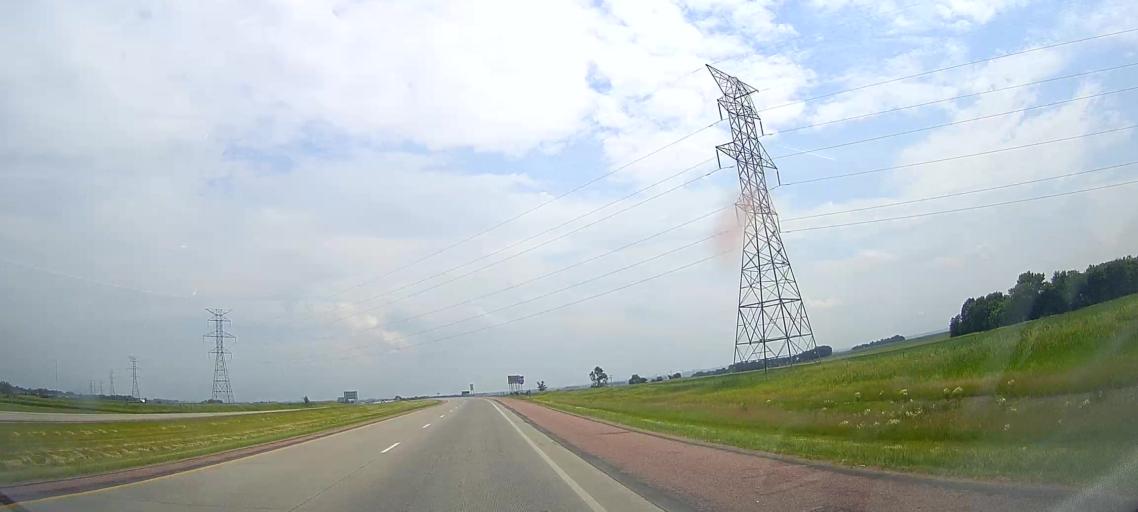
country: US
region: South Dakota
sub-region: Clay County
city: Vermillion
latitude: 42.7805
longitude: -96.7873
